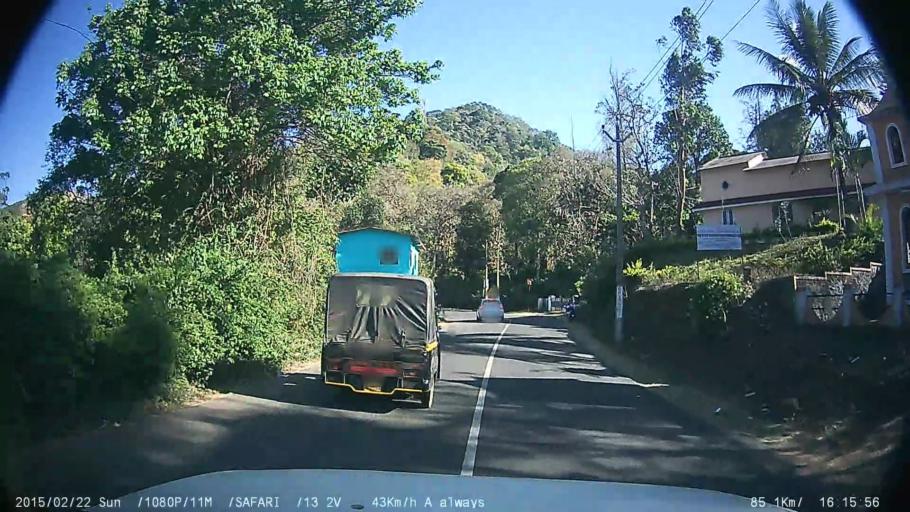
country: IN
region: Tamil Nadu
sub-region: Theni
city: Gudalur
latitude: 9.5831
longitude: 77.1083
